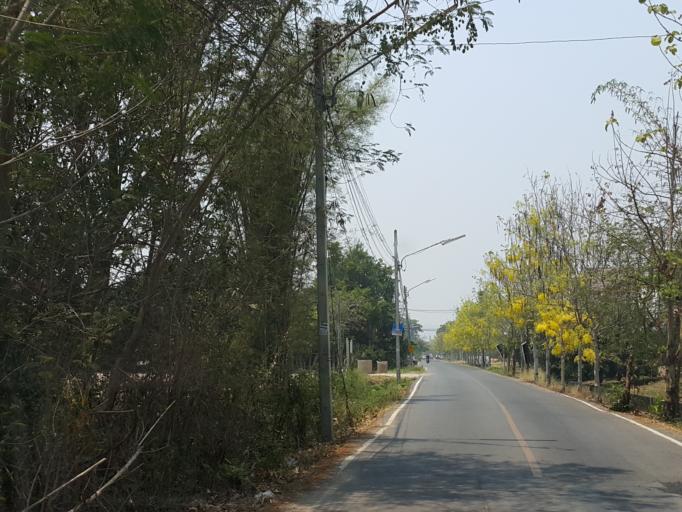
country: TH
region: Chiang Mai
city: Chiang Mai
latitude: 18.7527
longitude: 98.9738
